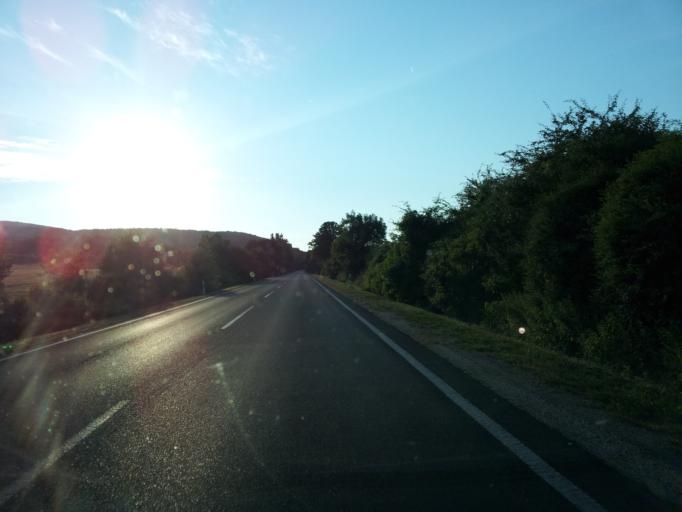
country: HU
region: Fejer
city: Szarliget
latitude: 47.4995
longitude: 18.5036
